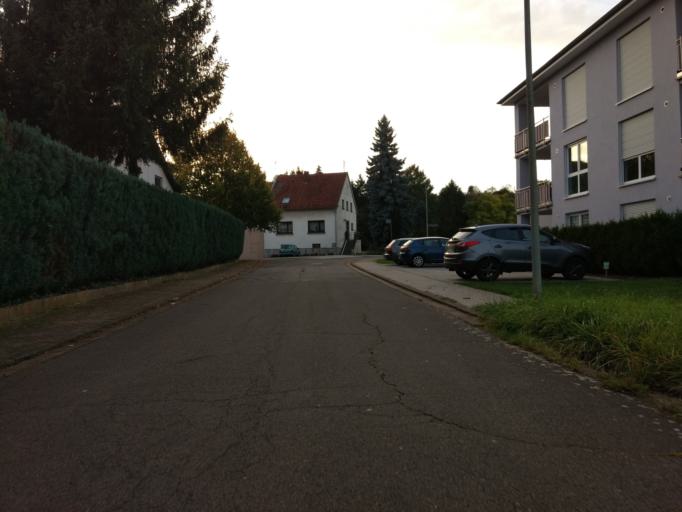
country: DE
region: Saarland
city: Rehlingen-Siersburg
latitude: 49.3756
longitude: 6.6771
